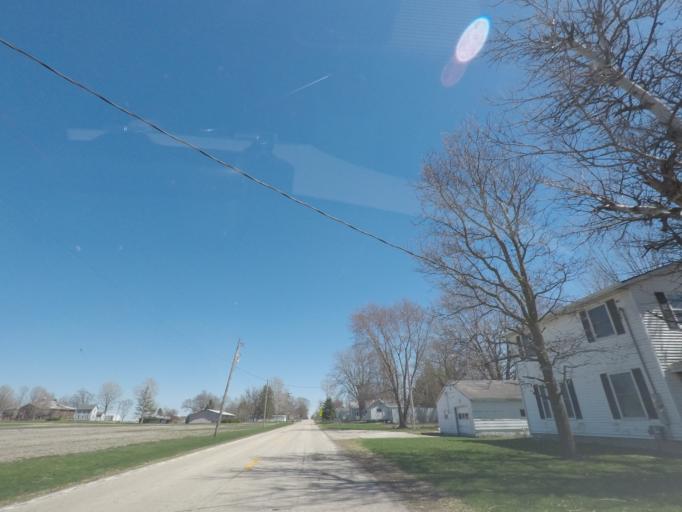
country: US
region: Illinois
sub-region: Macon County
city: Warrensburg
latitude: 39.9684
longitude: -89.1650
